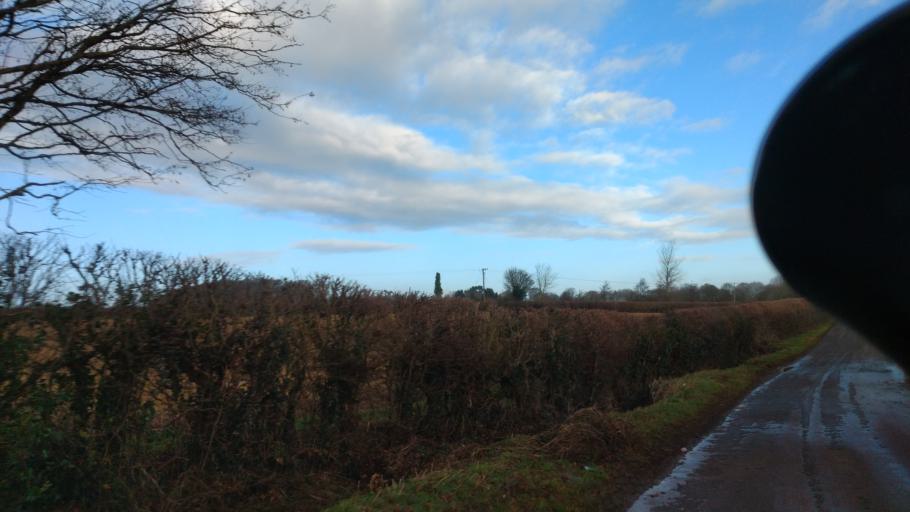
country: GB
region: England
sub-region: Wiltshire
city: Corsham
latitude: 51.4606
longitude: -2.1621
